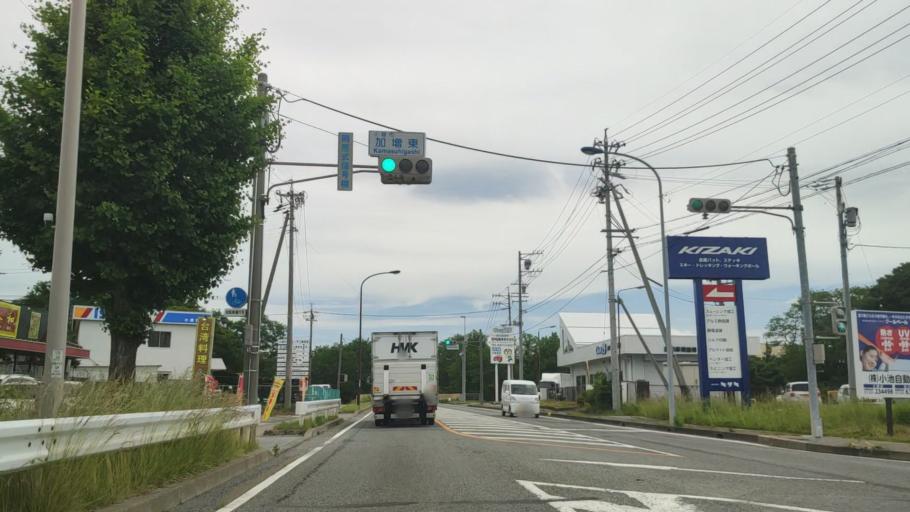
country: JP
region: Nagano
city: Komoro
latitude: 36.3161
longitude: 138.4443
